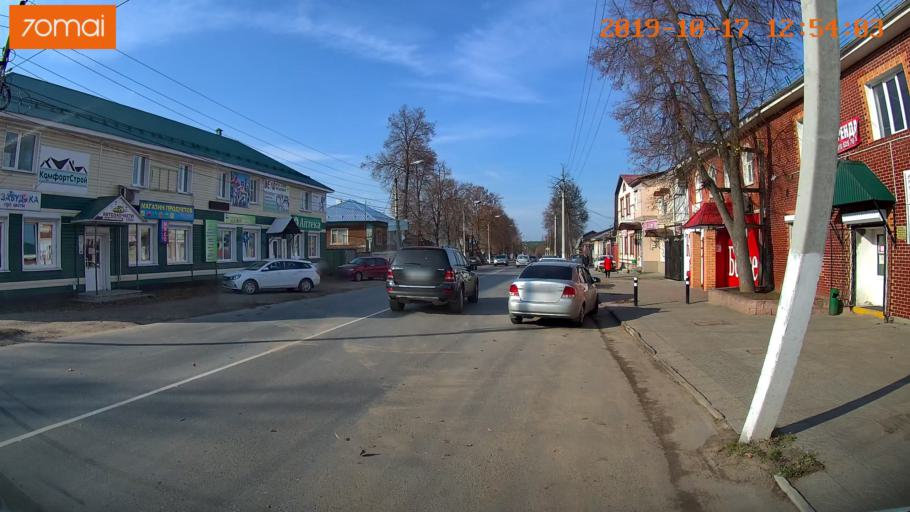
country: RU
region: Rjazan
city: Kasimov
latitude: 54.9423
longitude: 41.3801
